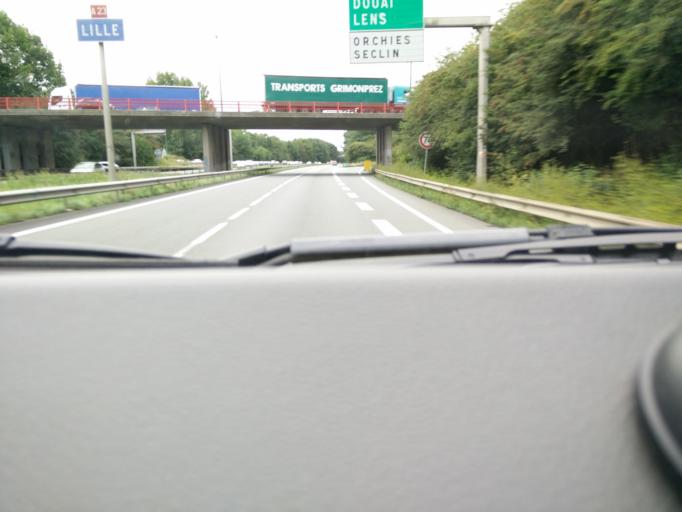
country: FR
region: Nord-Pas-de-Calais
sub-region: Departement du Nord
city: Orchies
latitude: 50.4708
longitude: 3.2287
